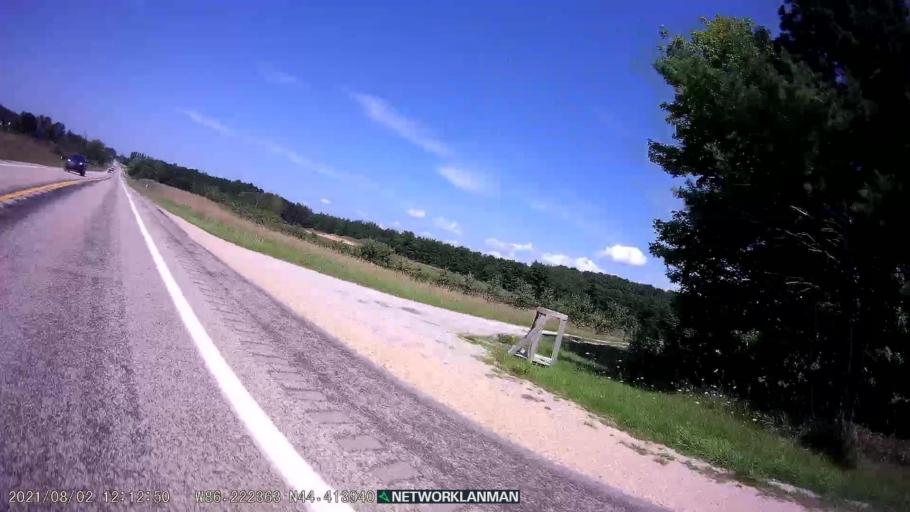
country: US
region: Michigan
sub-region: Manistee County
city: Manistee
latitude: 44.4142
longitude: -86.2224
